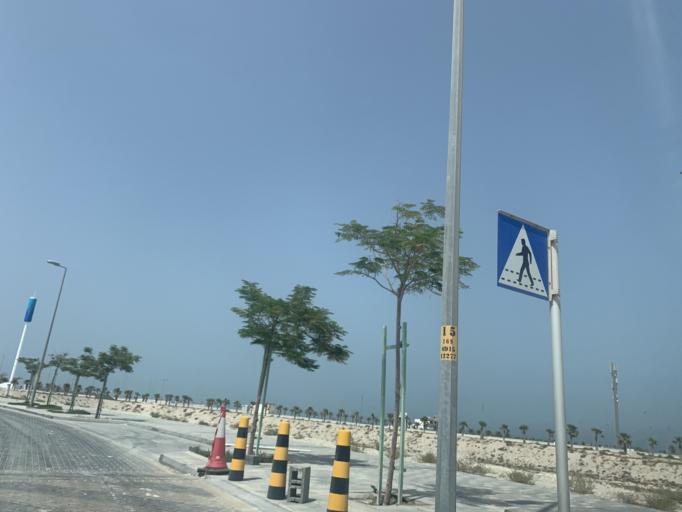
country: BH
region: Muharraq
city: Al Hadd
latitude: 26.2721
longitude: 50.6747
